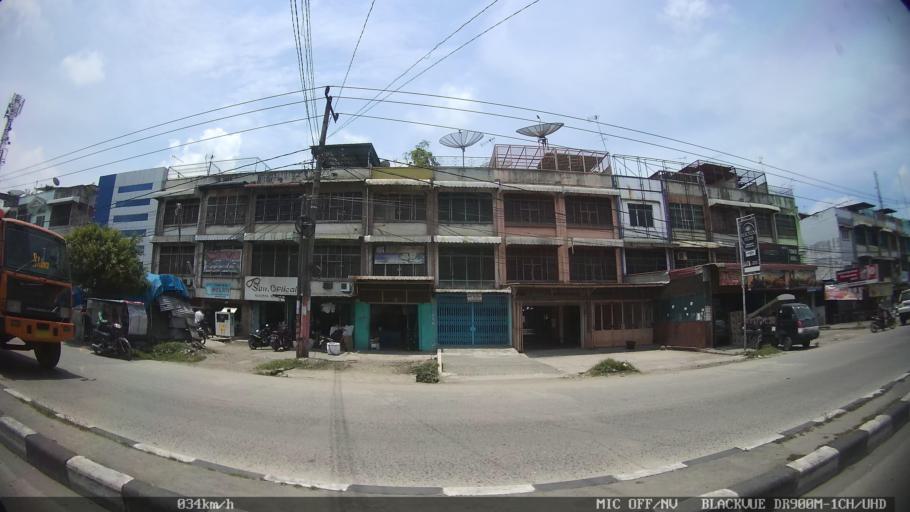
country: ID
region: North Sumatra
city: Labuhan Deli
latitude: 3.7227
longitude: 98.6796
